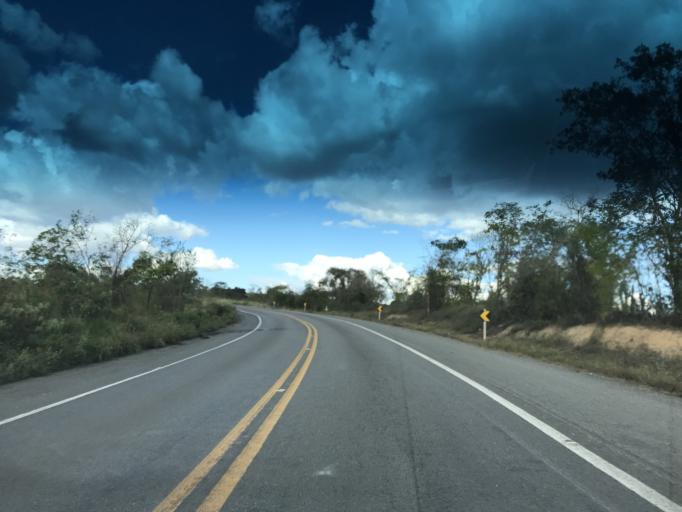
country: BR
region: Bahia
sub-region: Ruy Barbosa
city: Terra Nova
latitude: -12.4461
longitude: -40.8588
